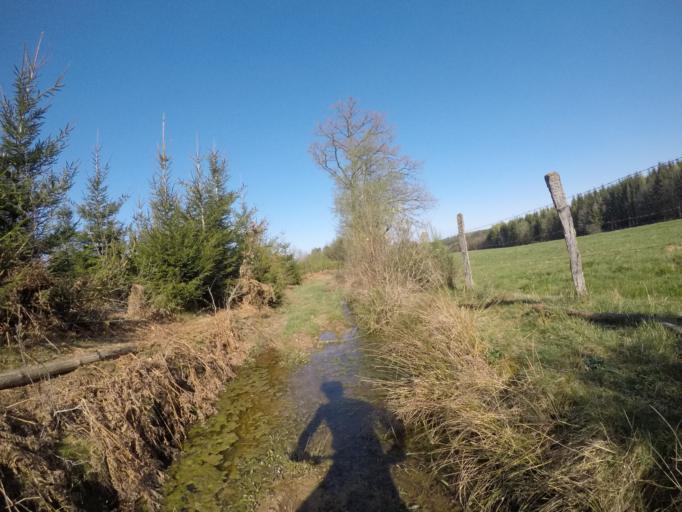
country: BE
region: Wallonia
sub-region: Province du Luxembourg
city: Leglise
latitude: 49.7989
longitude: 5.5795
